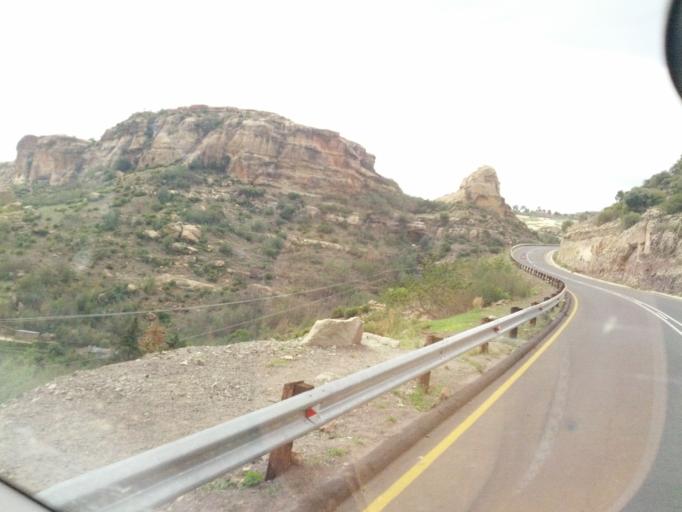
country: LS
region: Maseru
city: Nako
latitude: -29.4792
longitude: 27.7394
